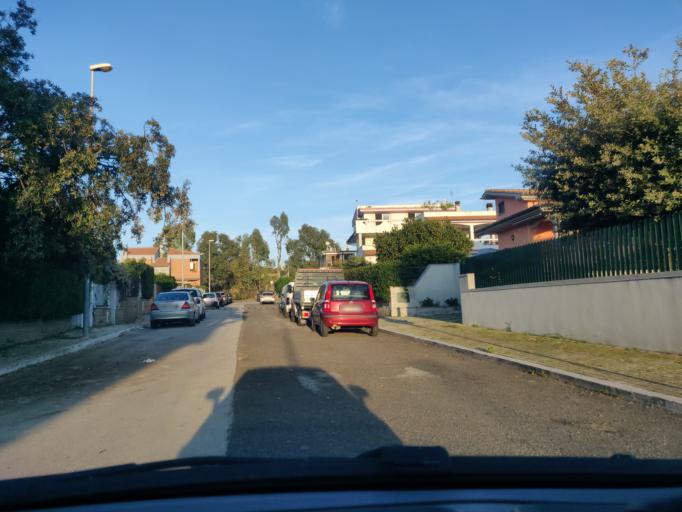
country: IT
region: Latium
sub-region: Citta metropolitana di Roma Capitale
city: Civitavecchia
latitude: 42.0632
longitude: 11.8203
